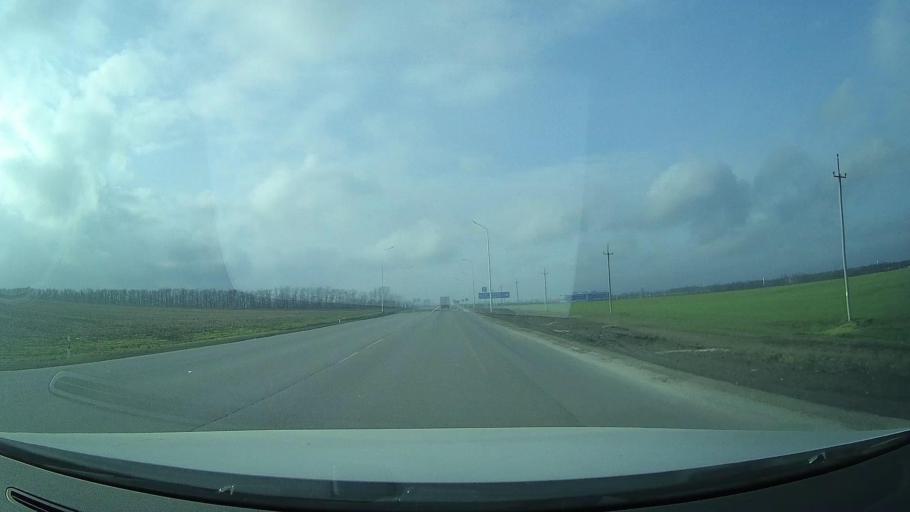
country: RU
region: Rostov
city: Grushevskaya
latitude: 47.3790
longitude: 39.8533
